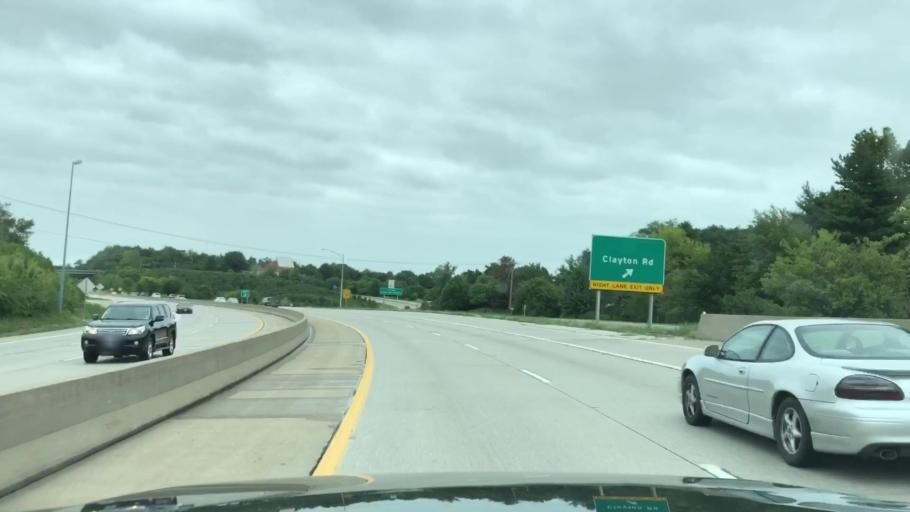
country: US
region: Missouri
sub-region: Saint Louis County
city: Manchester
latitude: 38.6199
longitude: -90.5104
